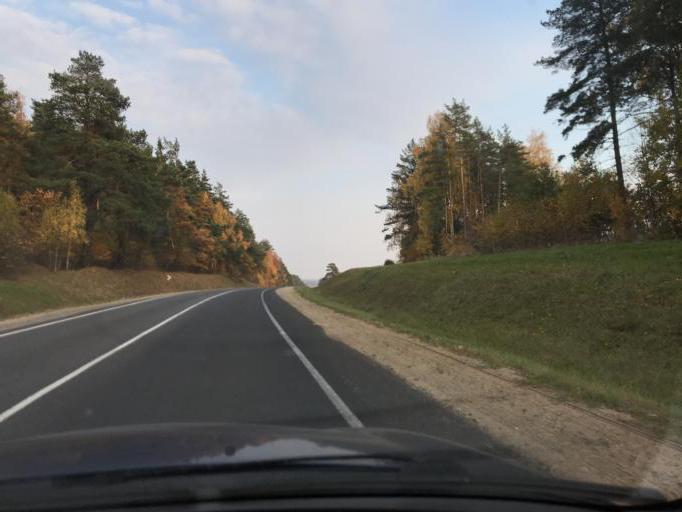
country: BY
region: Grodnenskaya
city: Navahrudak
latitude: 53.5919
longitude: 25.9289
